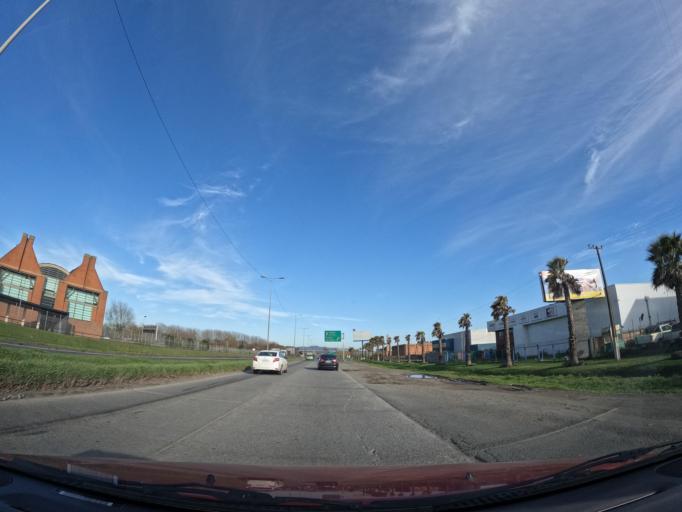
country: CL
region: Biobio
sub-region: Provincia de Concepcion
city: Concepcion
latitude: -36.7820
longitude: -73.0762
